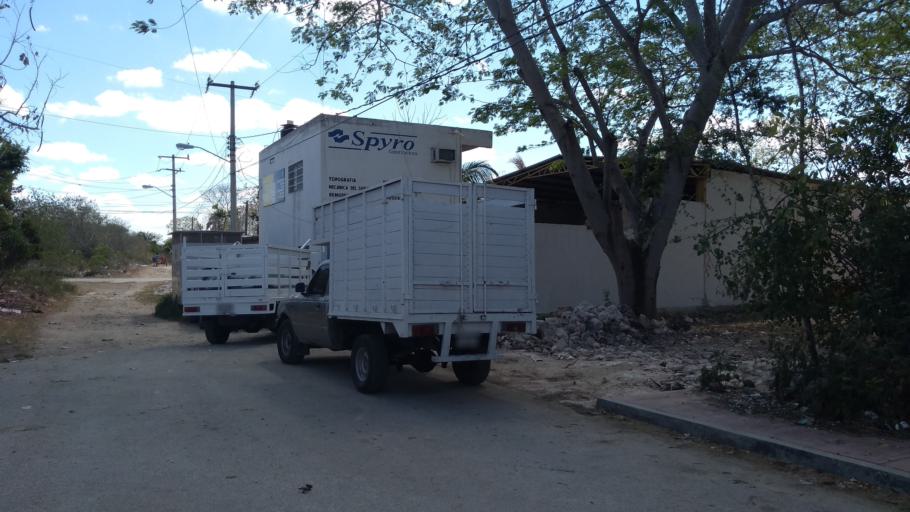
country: MX
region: Yucatan
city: Itzincab Palomeque
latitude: 20.9235
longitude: -89.6694
